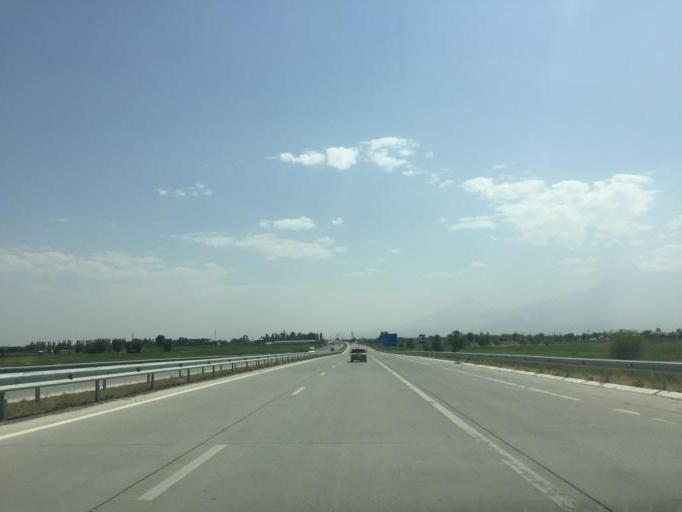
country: AM
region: Ararat
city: Arevabuyr
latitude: 40.0332
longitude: 44.4631
